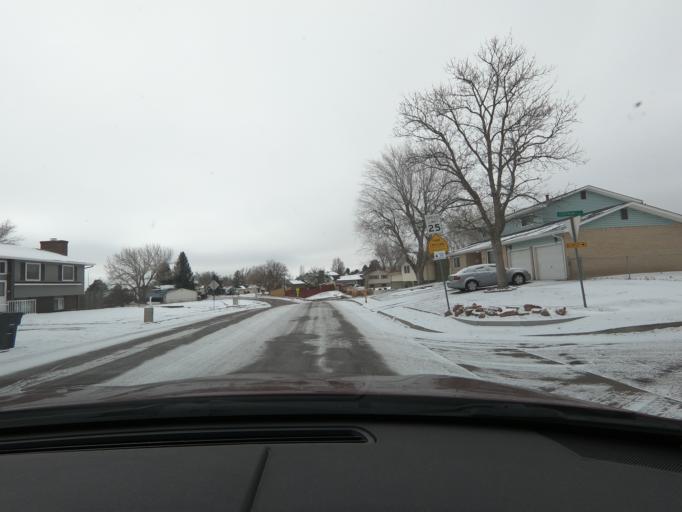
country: US
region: Colorado
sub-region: El Paso County
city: Security-Widefield
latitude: 38.7262
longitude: -104.6945
